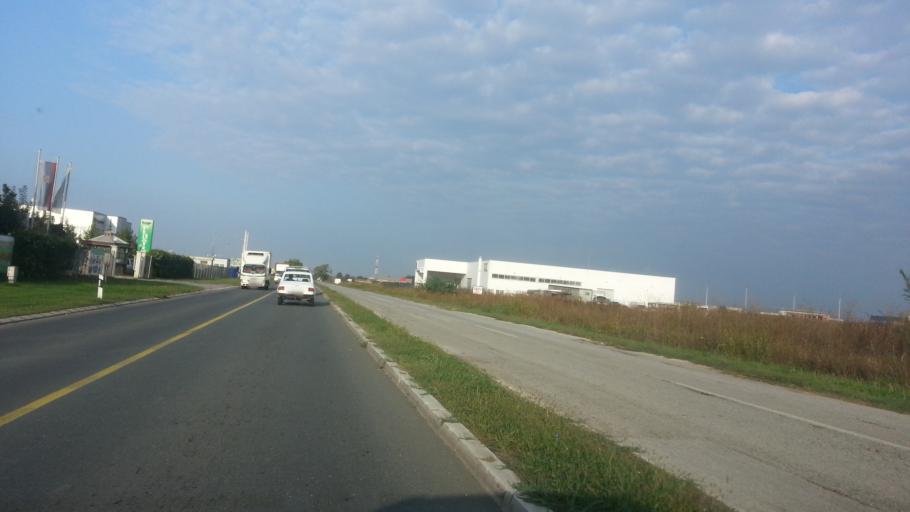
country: RS
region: Autonomna Pokrajina Vojvodina
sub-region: Sremski Okrug
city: Stara Pazova
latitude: 44.9866
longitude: 20.2018
